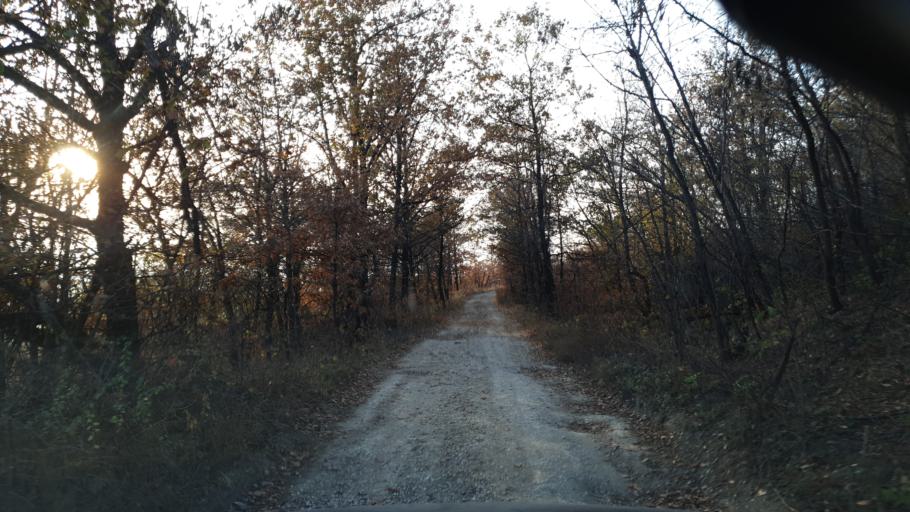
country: RS
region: Central Serbia
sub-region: Borski Okrug
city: Bor
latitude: 44.0683
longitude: 22.0767
